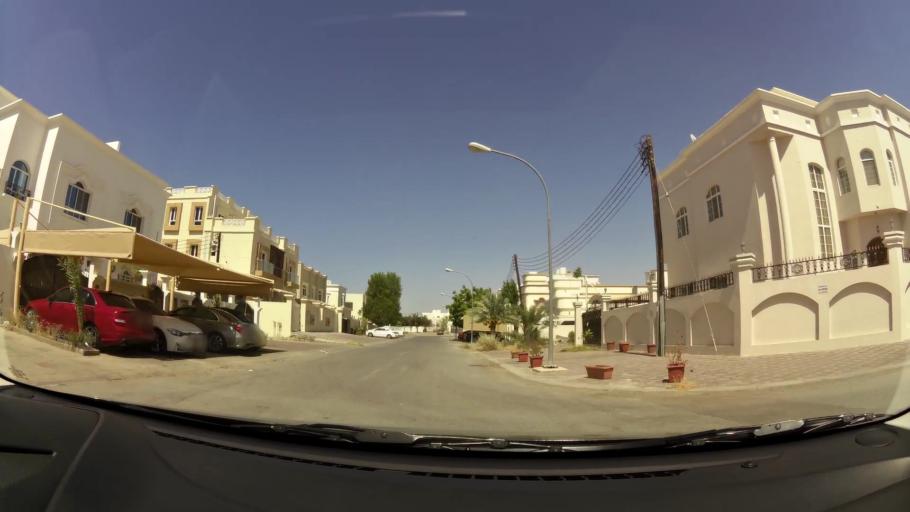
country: OM
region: Muhafazat Masqat
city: Bawshar
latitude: 23.5979
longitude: 58.3533
